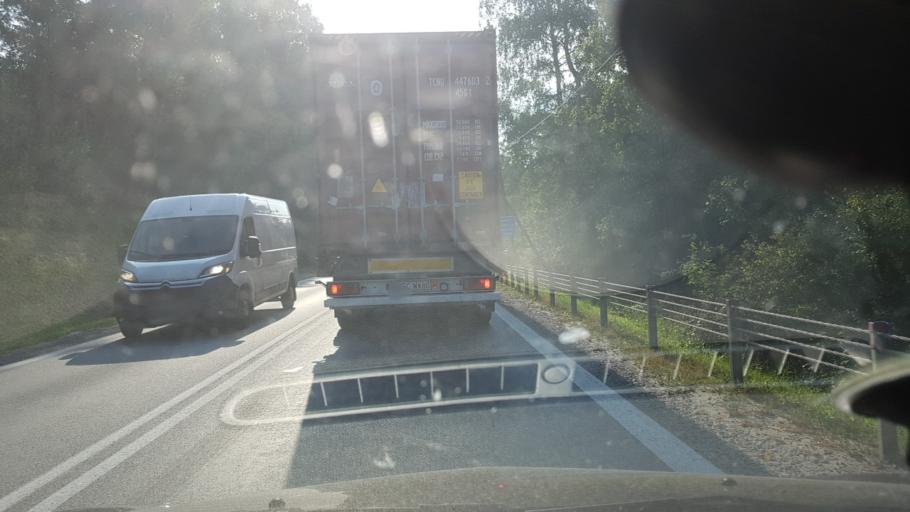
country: PL
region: Lesser Poland Voivodeship
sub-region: Powiat suski
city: Naprawa
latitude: 49.6539
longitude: 19.9033
